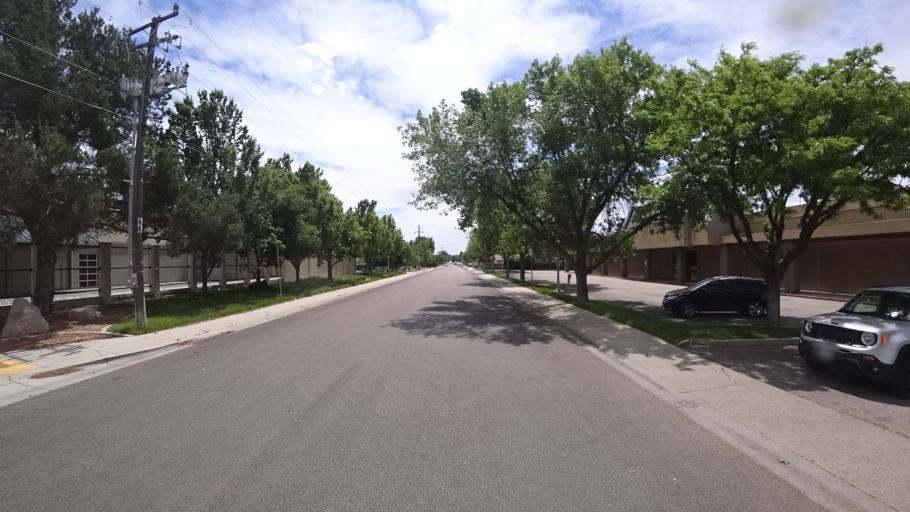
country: US
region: Idaho
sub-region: Ada County
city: Garden City
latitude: 43.6185
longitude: -116.3092
